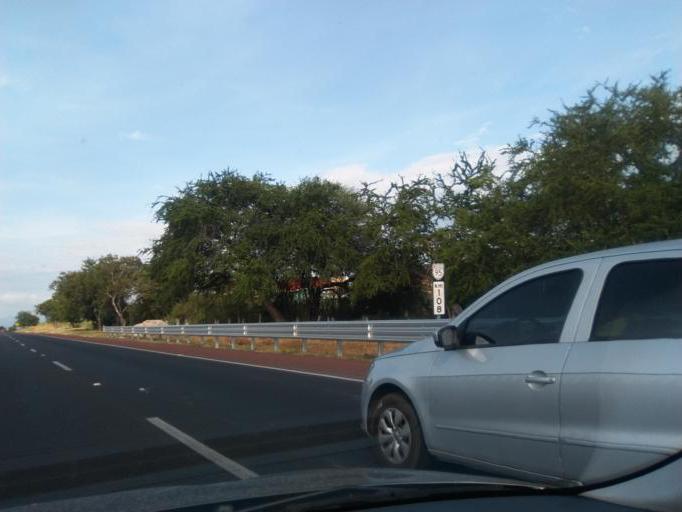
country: MX
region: Morelos
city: Xochitepec
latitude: 18.7737
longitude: -99.2254
